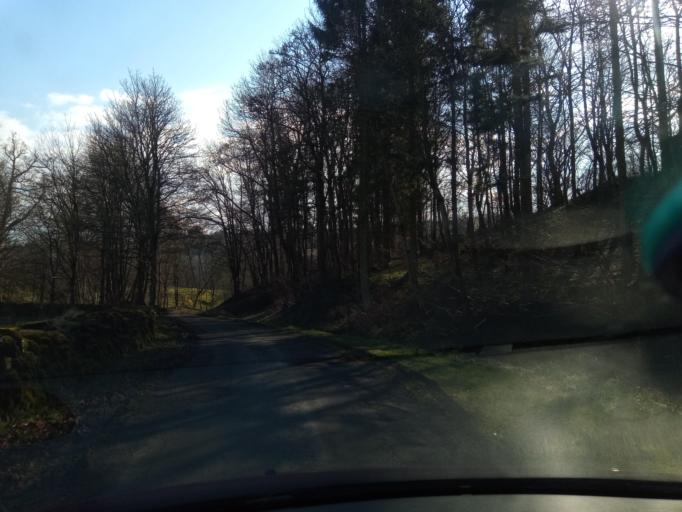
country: GB
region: Scotland
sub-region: The Scottish Borders
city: Hawick
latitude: 55.4186
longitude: -2.8153
